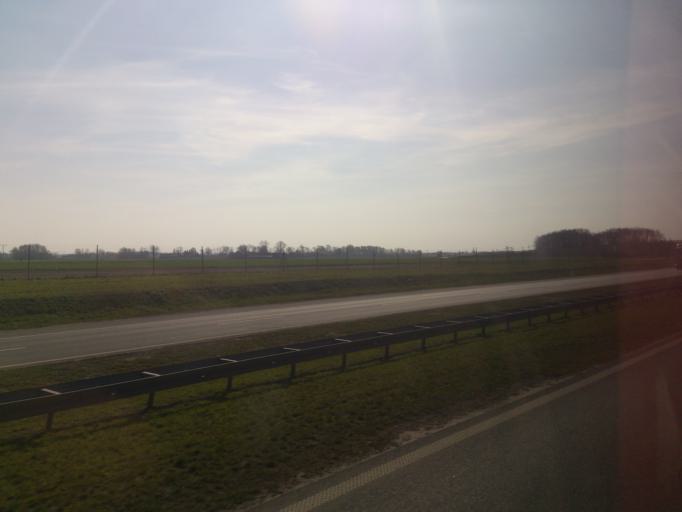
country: PL
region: Lodz Voivodeship
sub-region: Powiat kutnowski
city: Lanieta
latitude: 52.4155
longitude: 19.2639
